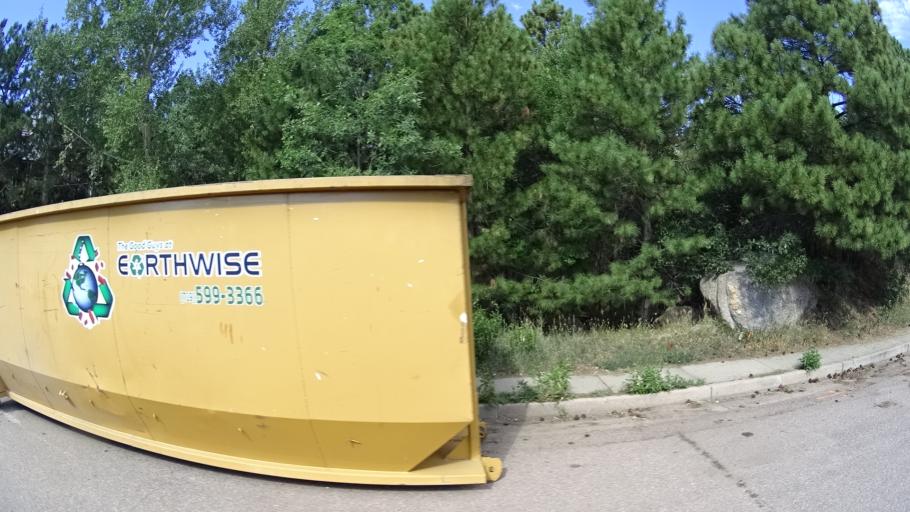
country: US
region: Colorado
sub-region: El Paso County
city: Fort Carson
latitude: 38.7584
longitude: -104.8324
